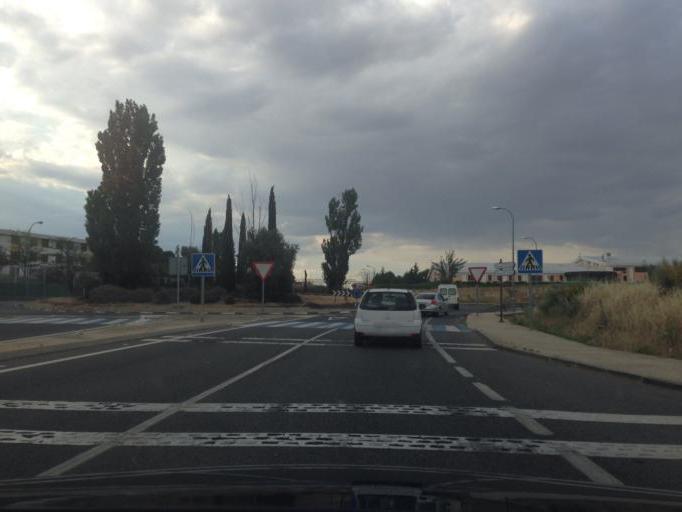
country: ES
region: Madrid
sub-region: Provincia de Madrid
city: Ajalvir
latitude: 40.5028
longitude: -3.4795
